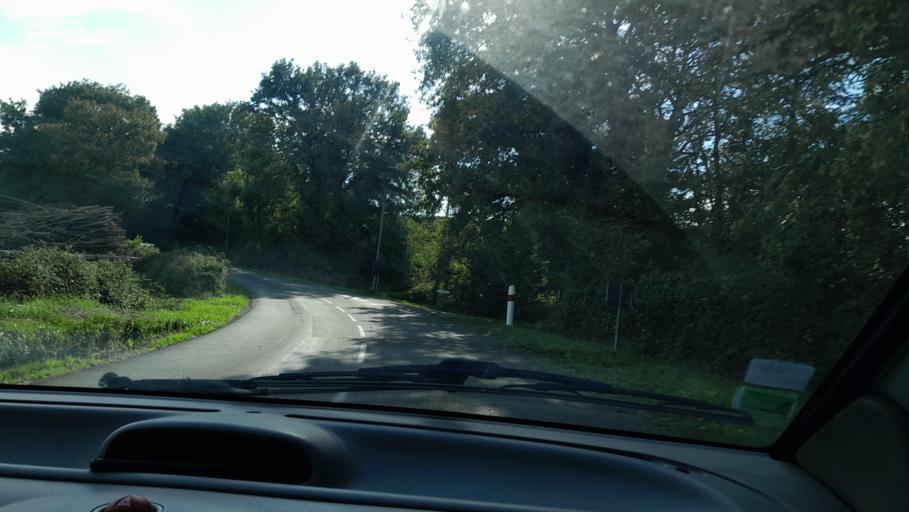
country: FR
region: Pays de la Loire
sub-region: Departement de la Mayenne
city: Saint-Berthevin
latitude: 48.0439
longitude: -0.8217
